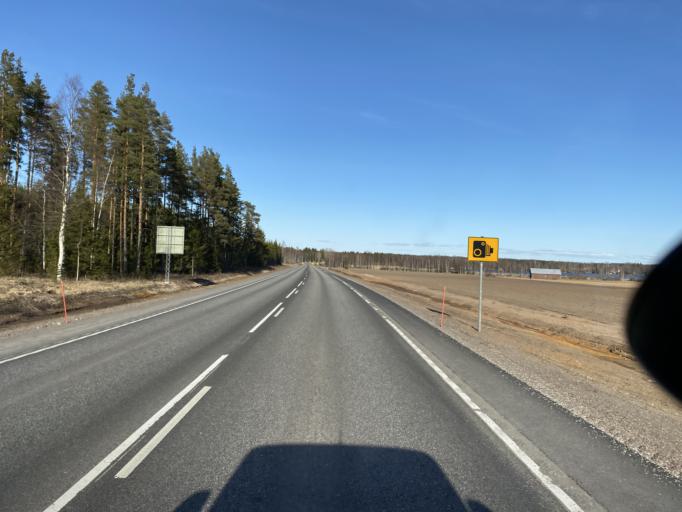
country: FI
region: Satakunta
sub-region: Rauma
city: Koeylioe
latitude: 61.1588
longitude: 22.2925
